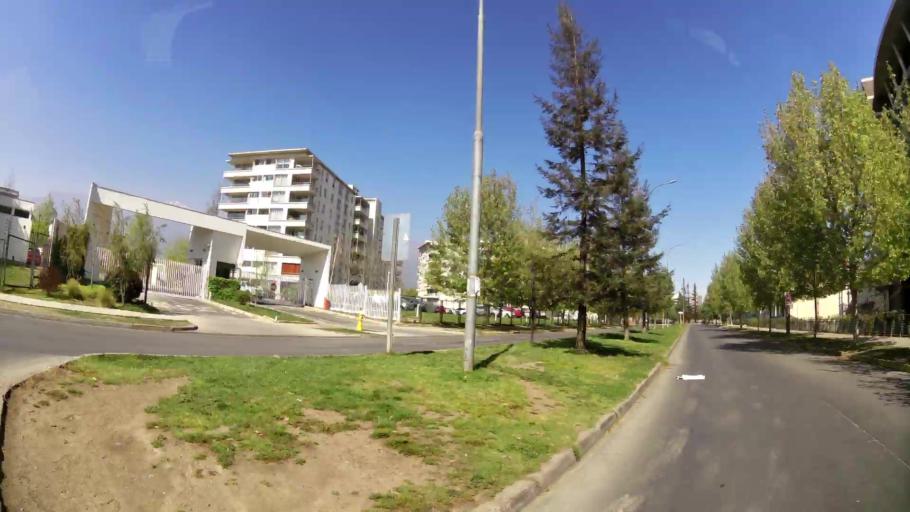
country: CL
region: Santiago Metropolitan
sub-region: Provincia de Santiago
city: Villa Presidente Frei, Nunoa, Santiago, Chile
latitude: -33.4871
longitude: -70.5768
